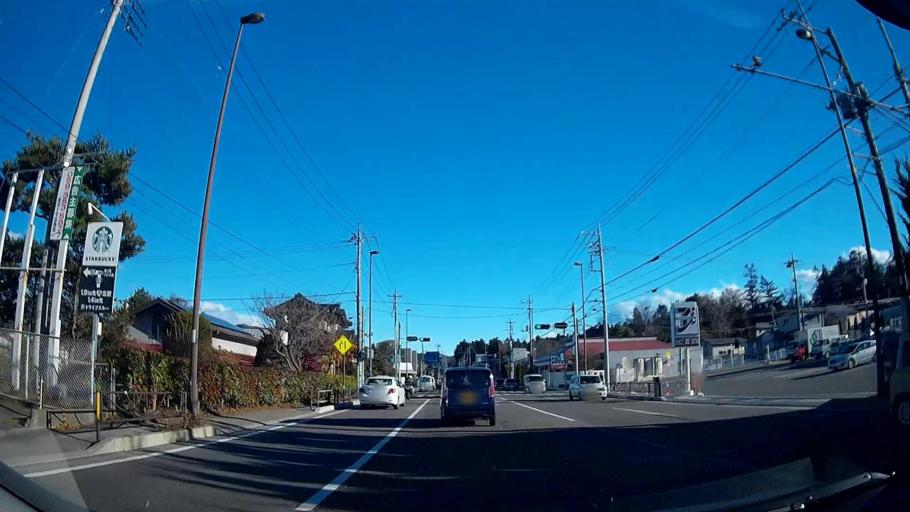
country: JP
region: Yamanashi
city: Fujikawaguchiko
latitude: 35.4759
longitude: 138.7904
